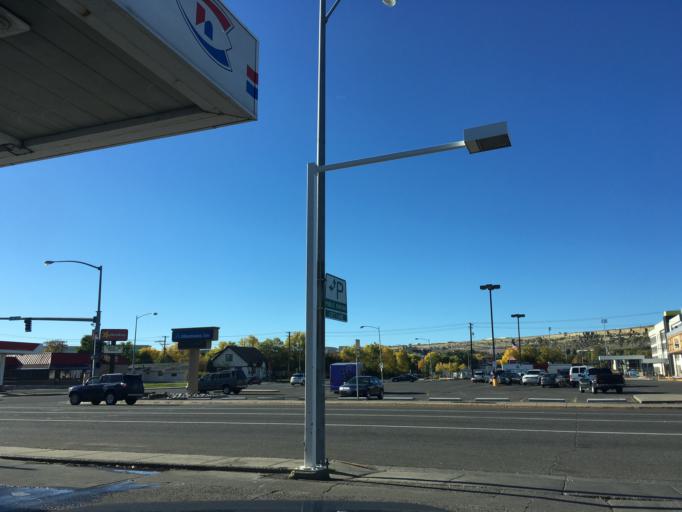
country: US
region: Montana
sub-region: Yellowstone County
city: Billings
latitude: 45.7871
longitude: -108.5082
